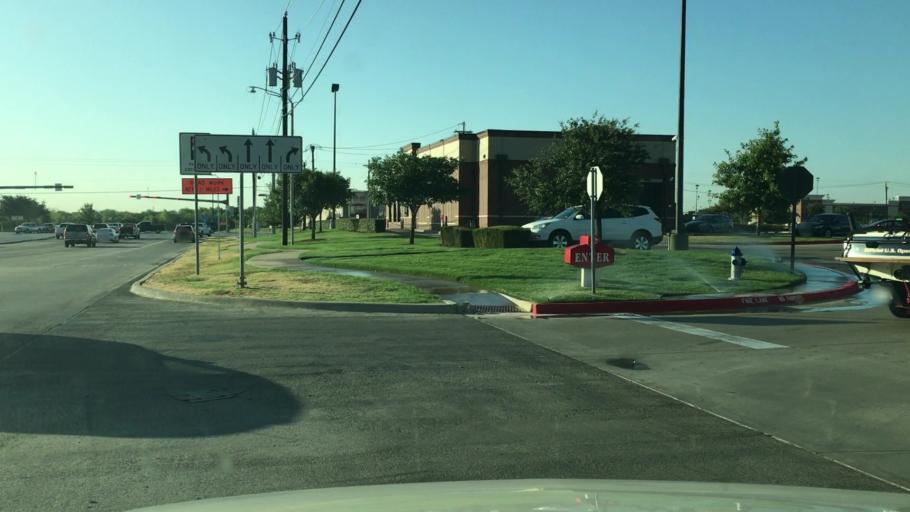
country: US
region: Texas
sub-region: Johnson County
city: Burleson
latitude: 32.5215
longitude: -97.3496
